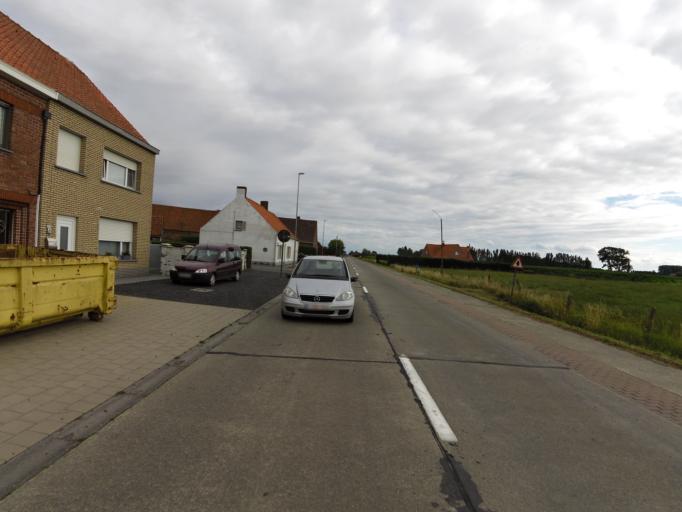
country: BE
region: Flanders
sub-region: Provincie West-Vlaanderen
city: Koekelare
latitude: 51.0817
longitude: 2.9857
